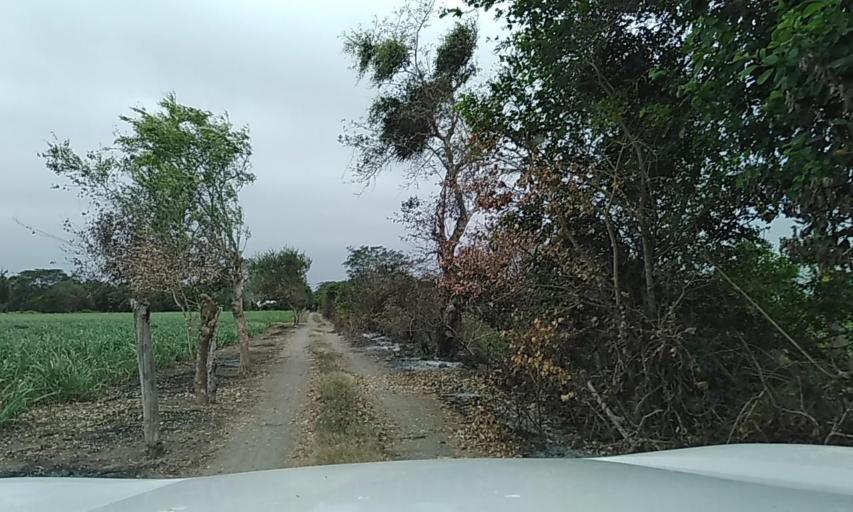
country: MX
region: Veracruz
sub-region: La Antigua
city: Nicolas Blanco (San Pancho)
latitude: 19.3030
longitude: -96.3177
